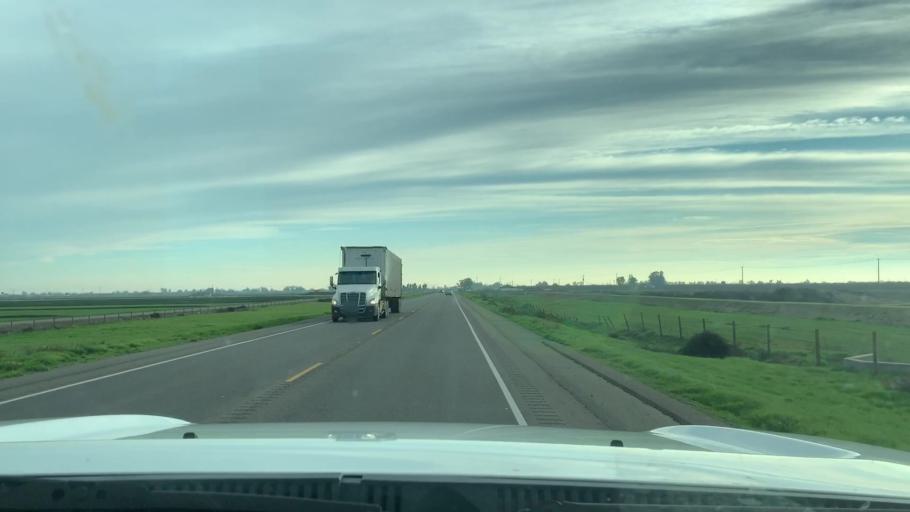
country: US
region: California
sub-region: Fresno County
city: Riverdale
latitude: 36.4561
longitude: -119.7965
